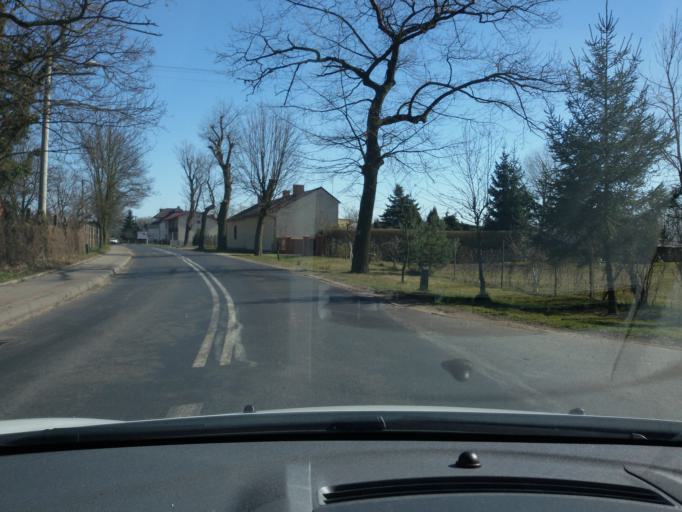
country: PL
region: Greater Poland Voivodeship
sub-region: Powiat gostynski
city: Poniec
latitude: 51.7543
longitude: 16.8399
